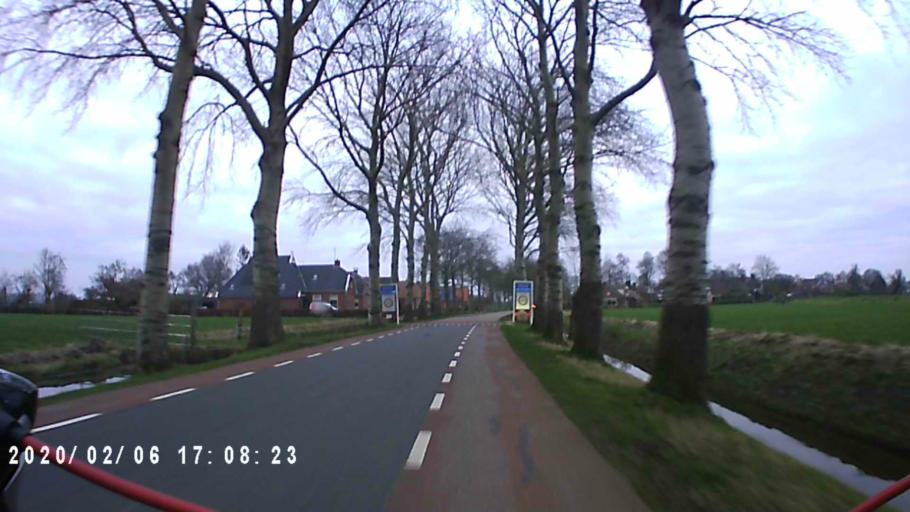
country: NL
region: Groningen
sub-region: Gemeente Winsum
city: Winsum
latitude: 53.2751
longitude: 6.5265
